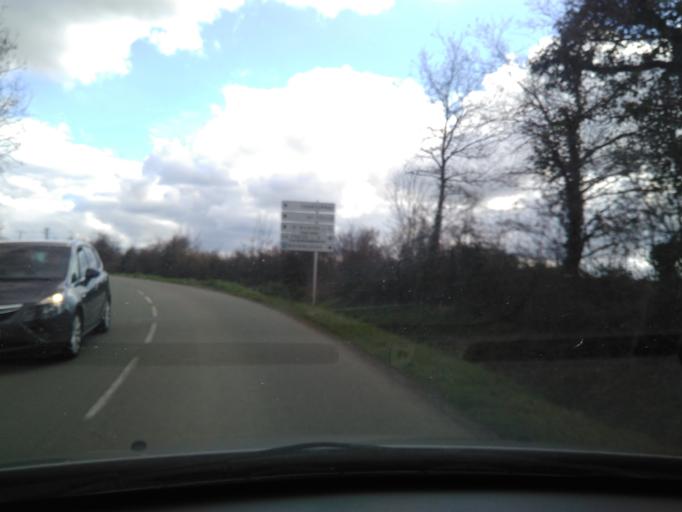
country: FR
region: Pays de la Loire
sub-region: Departement de la Vendee
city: Saint-Martin-des-Noyers
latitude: 46.6926
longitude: -1.1341
